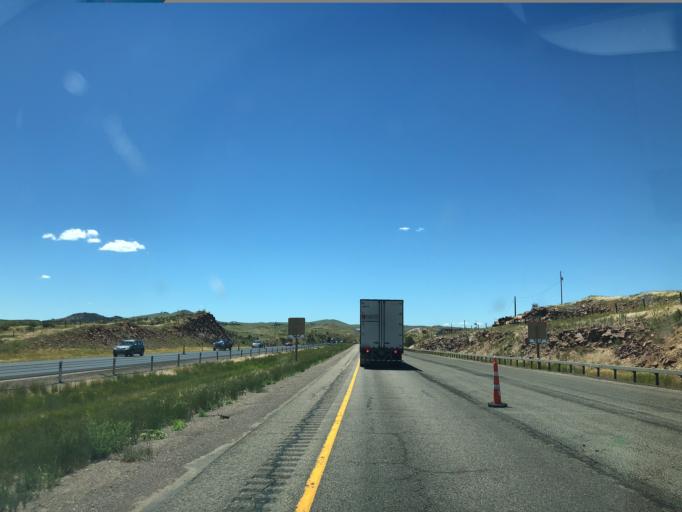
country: US
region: Wyoming
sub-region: Laramie County
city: Cheyenne
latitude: 41.0996
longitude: -105.1559
